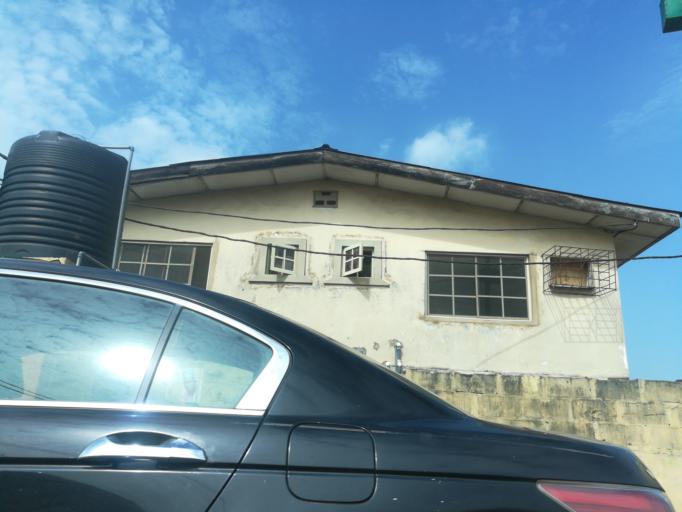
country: NG
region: Lagos
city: Ojota
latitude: 6.5784
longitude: 3.3702
